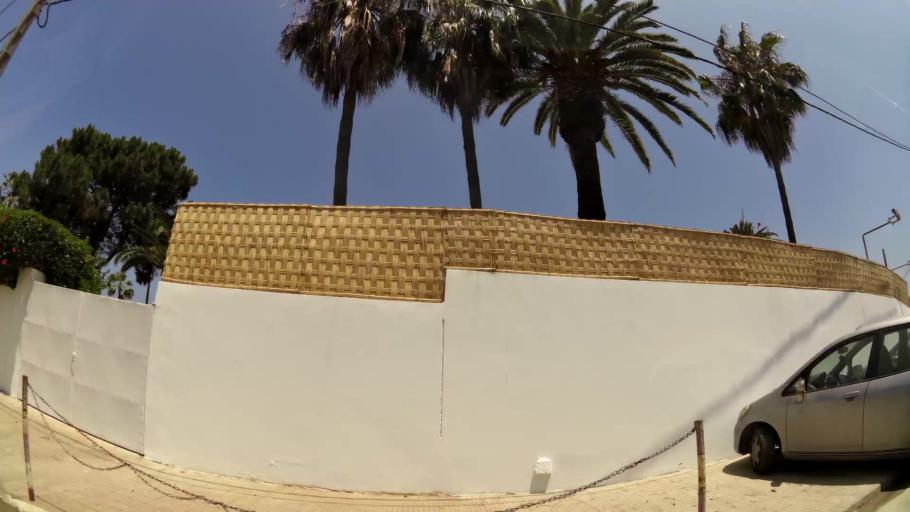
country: MA
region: Rabat-Sale-Zemmour-Zaer
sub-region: Rabat
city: Rabat
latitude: 34.0134
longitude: -6.8212
